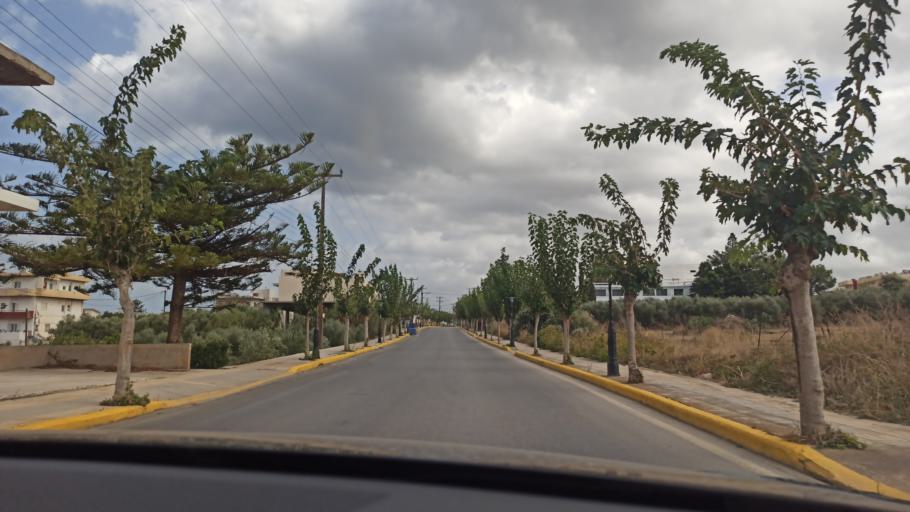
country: GR
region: Crete
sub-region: Nomos Irakleiou
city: Gazi
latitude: 35.3352
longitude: 25.0599
